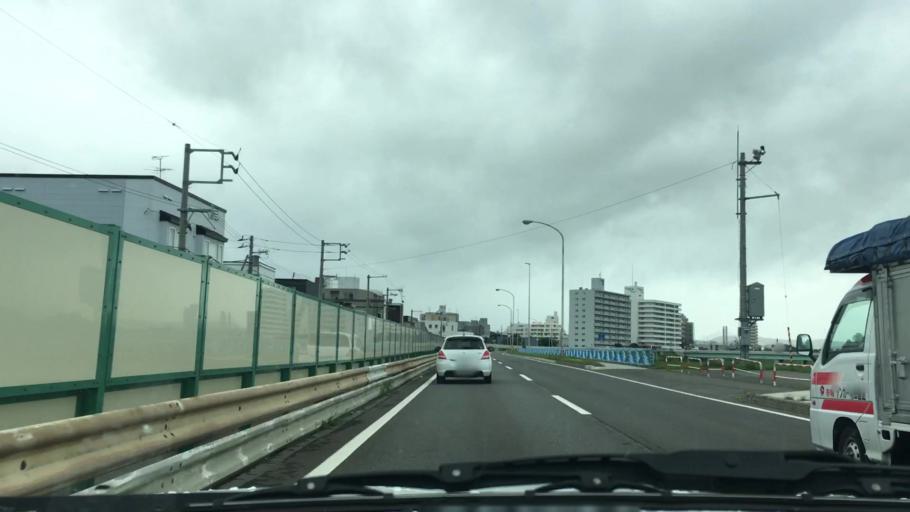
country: JP
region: Hokkaido
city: Sapporo
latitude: 43.0332
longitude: 141.3571
